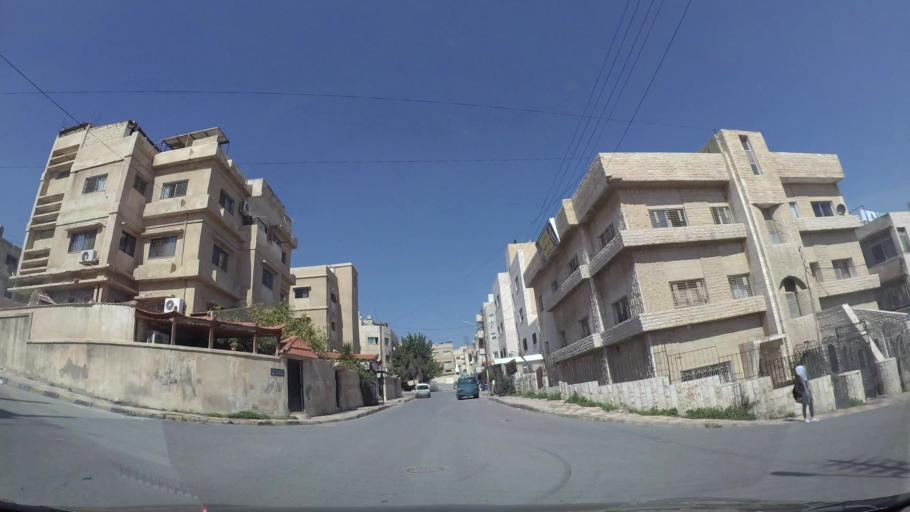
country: JO
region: Amman
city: Amman
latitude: 31.9791
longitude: 35.9925
